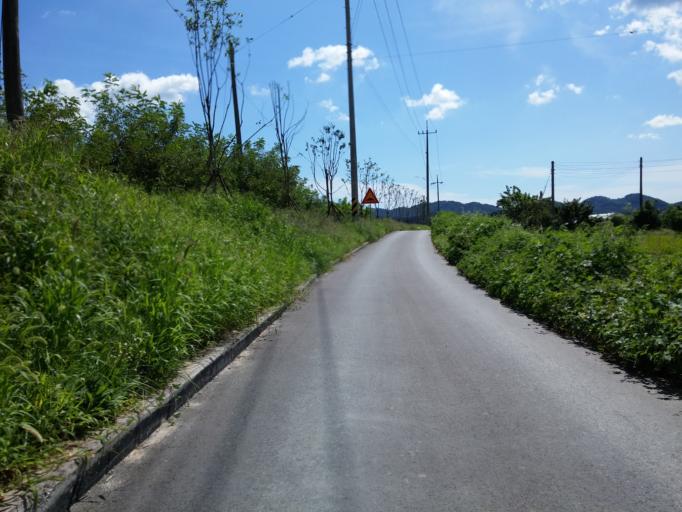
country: KR
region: Chungcheongbuk-do
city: Cheongju-si
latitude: 36.5943
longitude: 127.4969
